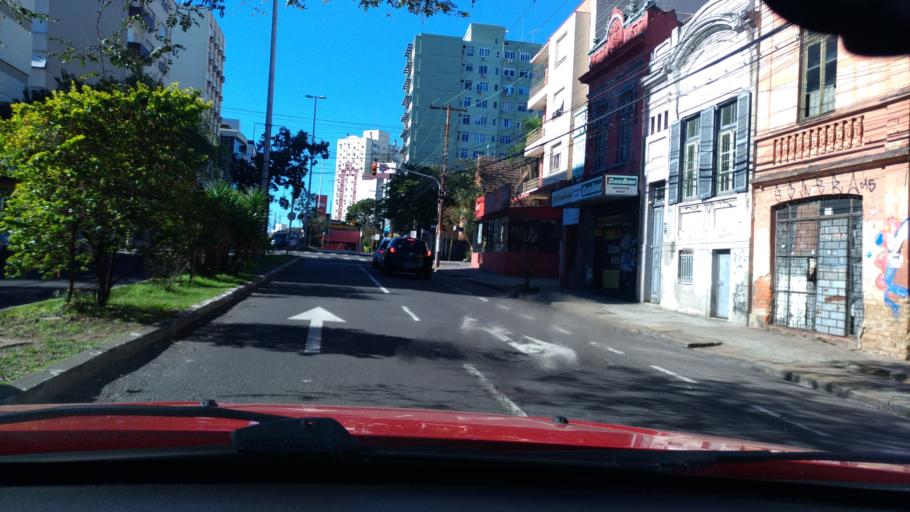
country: BR
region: Rio Grande do Sul
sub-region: Porto Alegre
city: Porto Alegre
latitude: -30.0195
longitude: -51.2063
